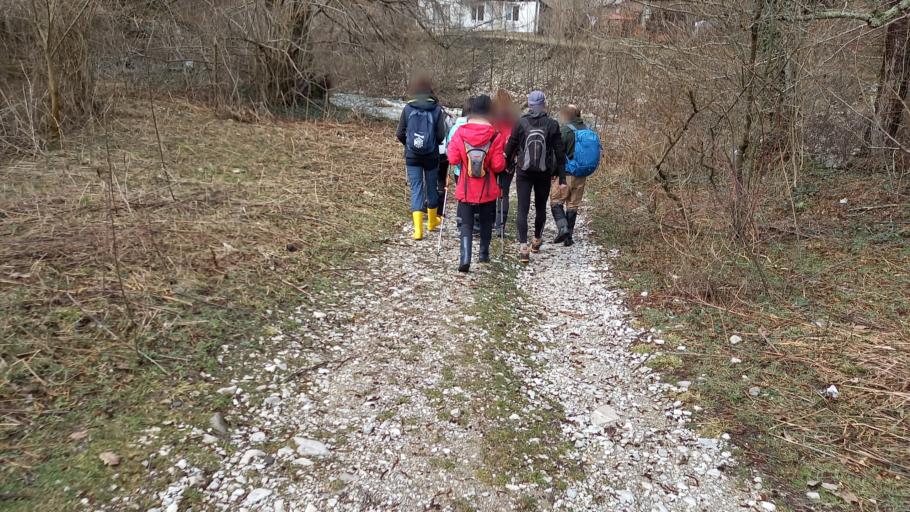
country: RU
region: Krasnodarskiy
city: Dzhubga
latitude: 44.4113
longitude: 38.7180
